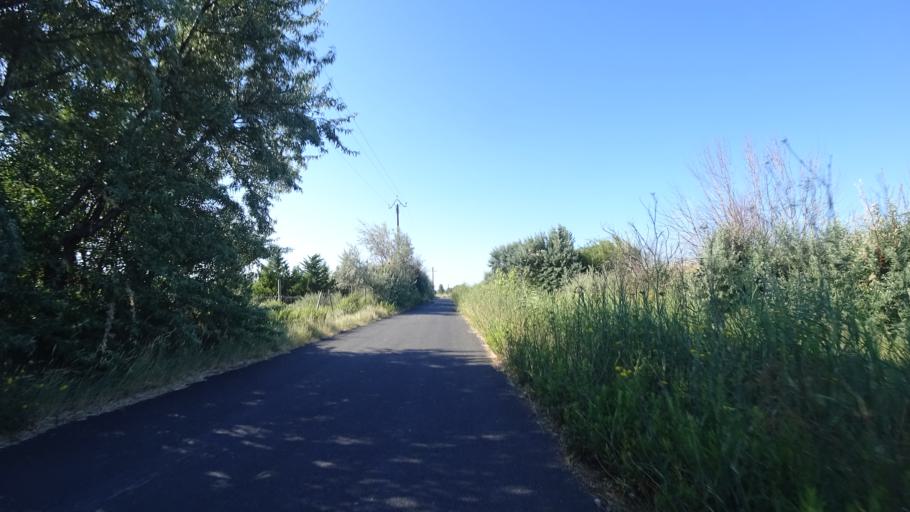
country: FR
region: Languedoc-Roussillon
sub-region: Departement des Pyrenees-Orientales
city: Sainte-Marie-Plage
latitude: 42.7384
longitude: 3.0248
